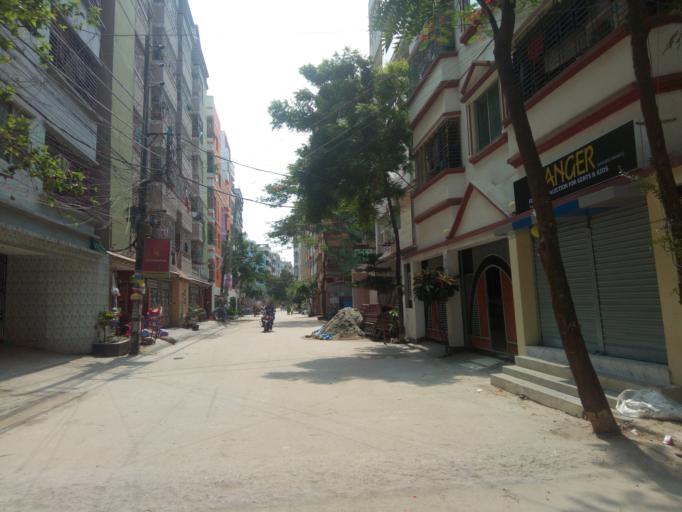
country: BD
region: Dhaka
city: Paltan
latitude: 23.7610
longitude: 90.4375
